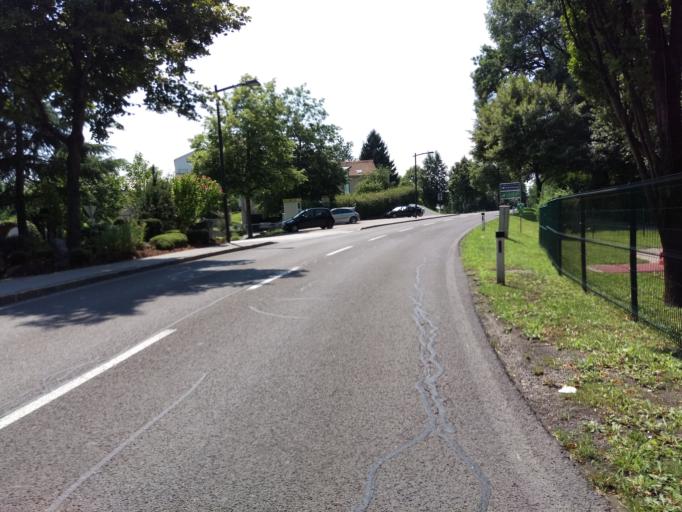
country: AT
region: Styria
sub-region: Politischer Bezirk Graz-Umgebung
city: Nestelbach bei Graz
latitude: 47.0738
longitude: 15.5920
